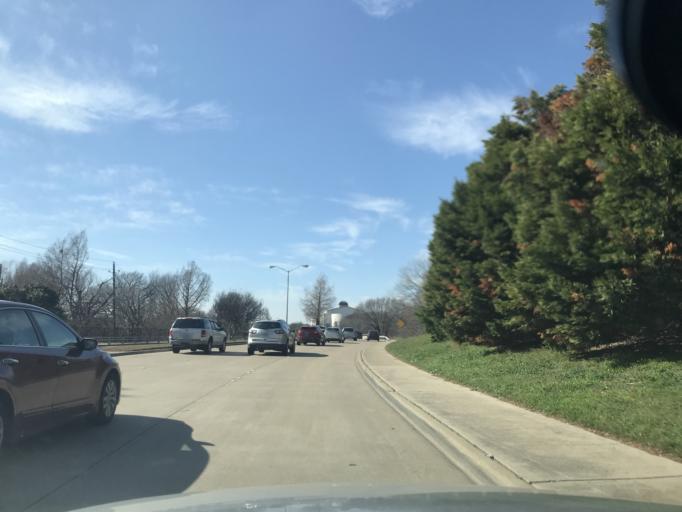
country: US
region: Texas
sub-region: Dallas County
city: Addison
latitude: 33.0426
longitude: -96.8066
